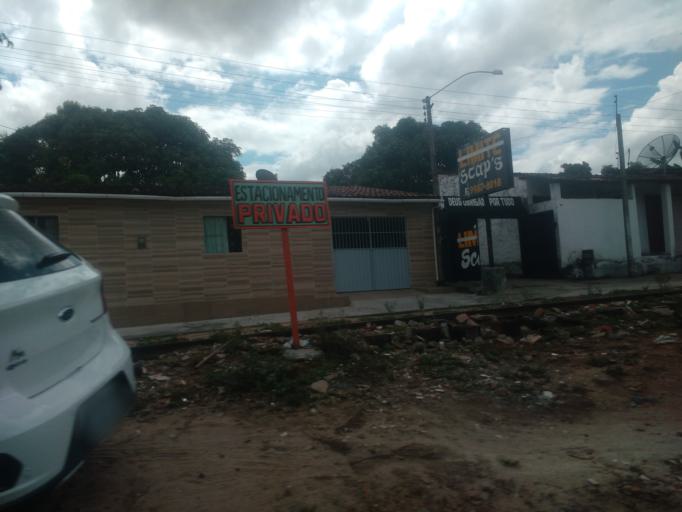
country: BR
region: Alagoas
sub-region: Uniao Dos Palmares
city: Uniao dos Palmares
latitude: -9.1637
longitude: -36.0298
